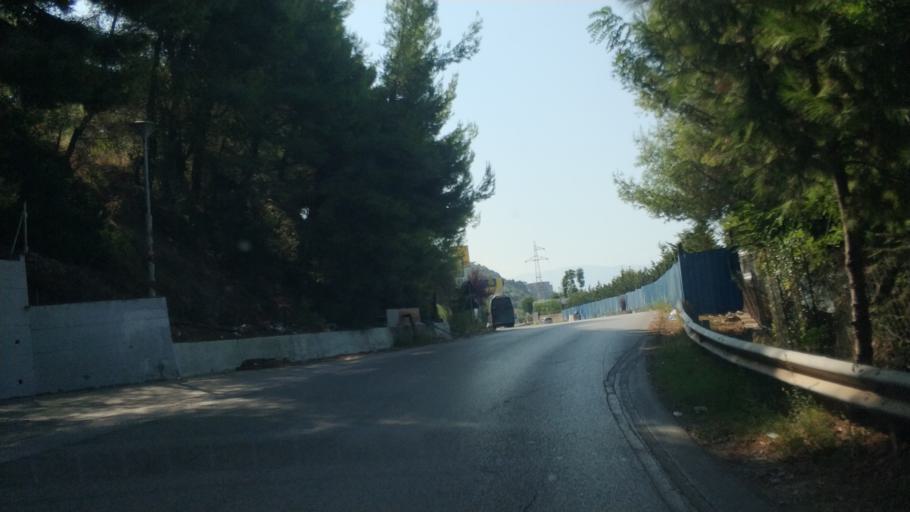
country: AL
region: Vlore
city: Vlore
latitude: 40.4046
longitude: 19.4803
